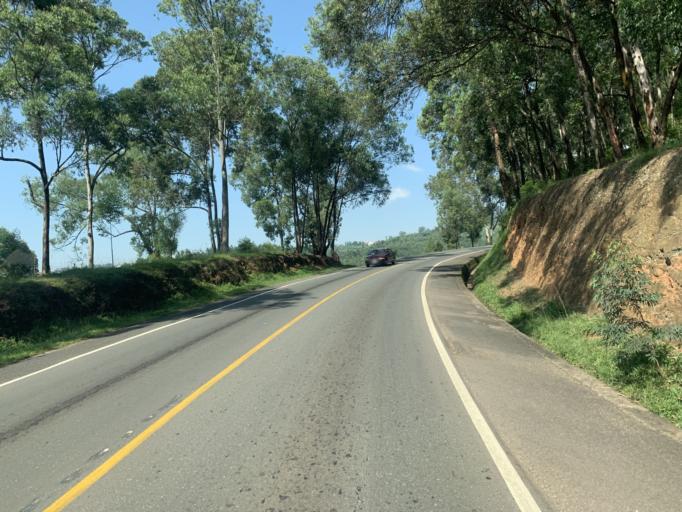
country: RW
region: Kigali
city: Kigali
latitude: -1.9945
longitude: 29.9265
